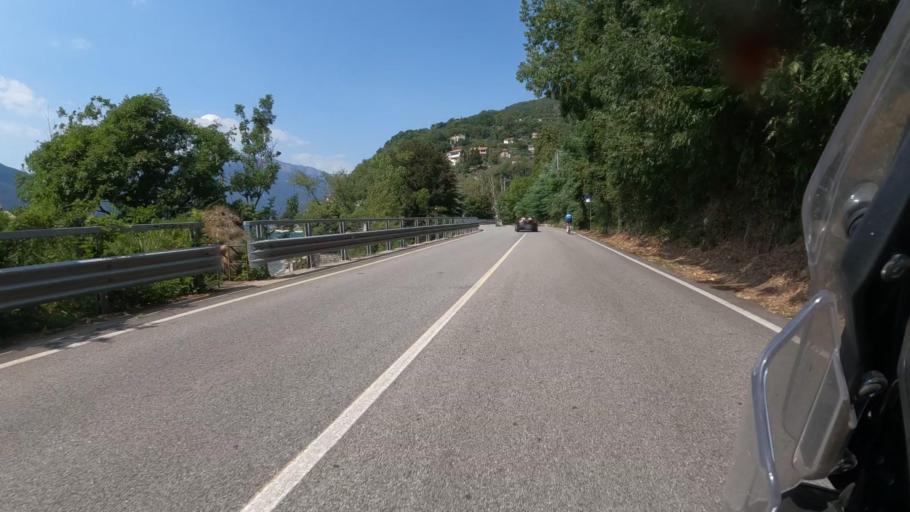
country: IT
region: Lombardy
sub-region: Provincia di Varese
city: Luino
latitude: 46.0223
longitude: 8.7519
